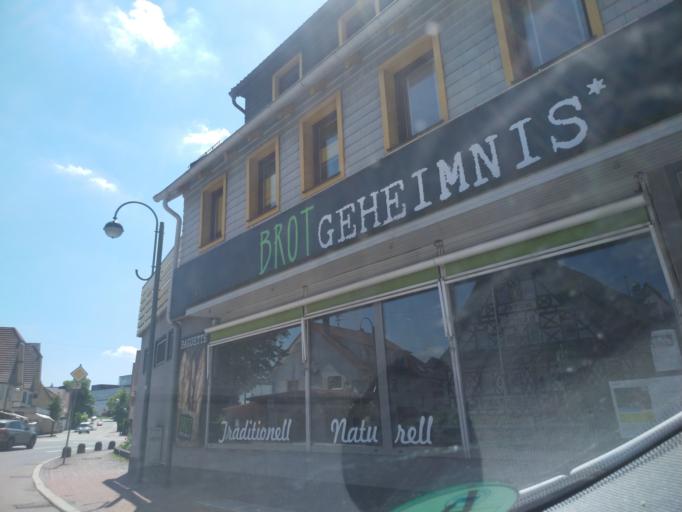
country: DE
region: Baden-Wuerttemberg
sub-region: Karlsruhe Region
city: Lossburg
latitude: 48.4115
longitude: 8.4531
